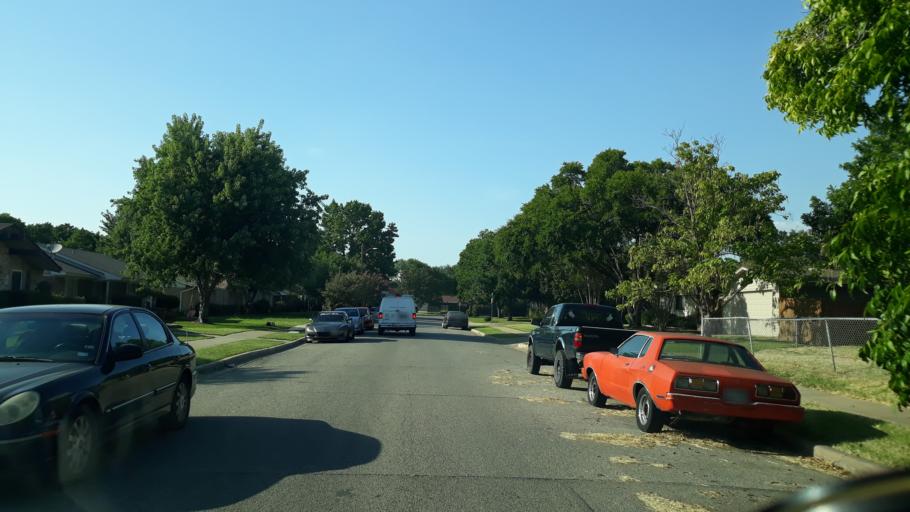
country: US
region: Texas
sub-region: Dallas County
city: Irving
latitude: 32.8486
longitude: -96.9982
